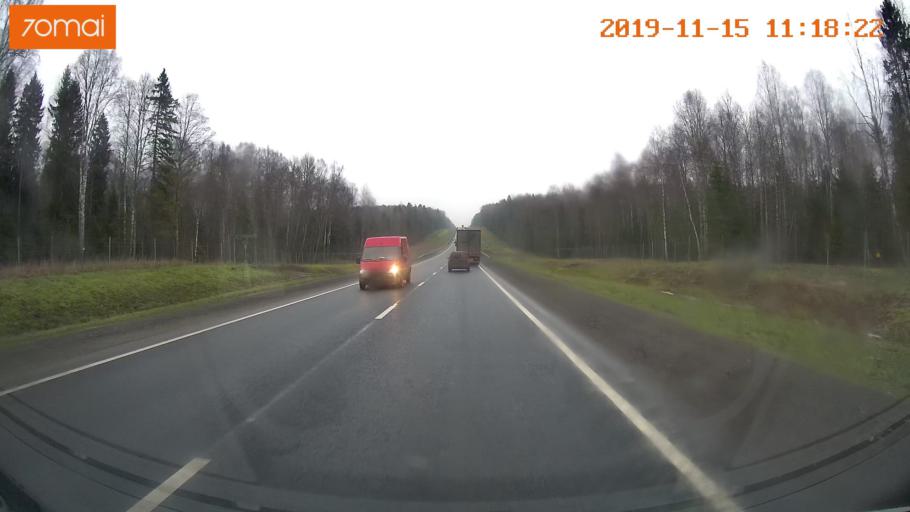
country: RU
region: Vologda
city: Molochnoye
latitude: 59.1356
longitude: 39.2700
